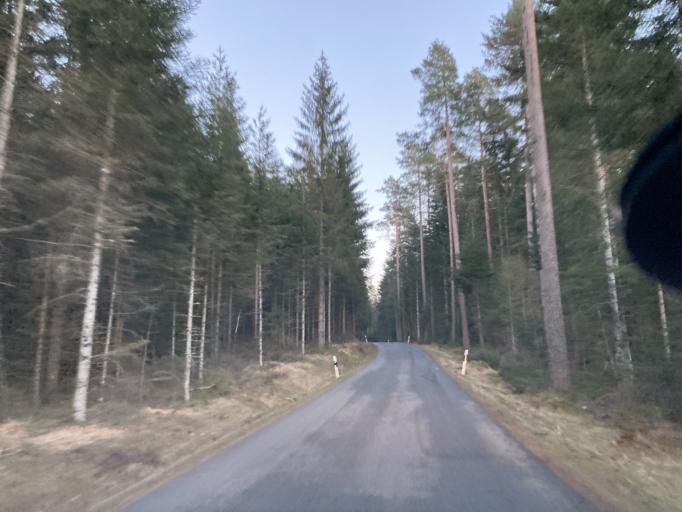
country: DE
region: Baden-Wuerttemberg
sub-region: Karlsruhe Region
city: Neuweiler
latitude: 48.6884
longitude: 8.5956
